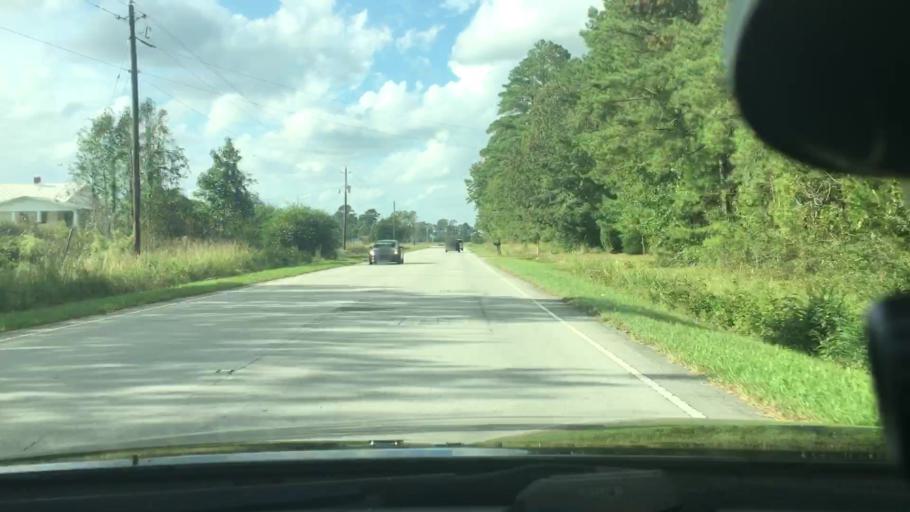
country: US
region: North Carolina
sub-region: Craven County
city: Vanceboro
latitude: 35.3699
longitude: -77.2061
